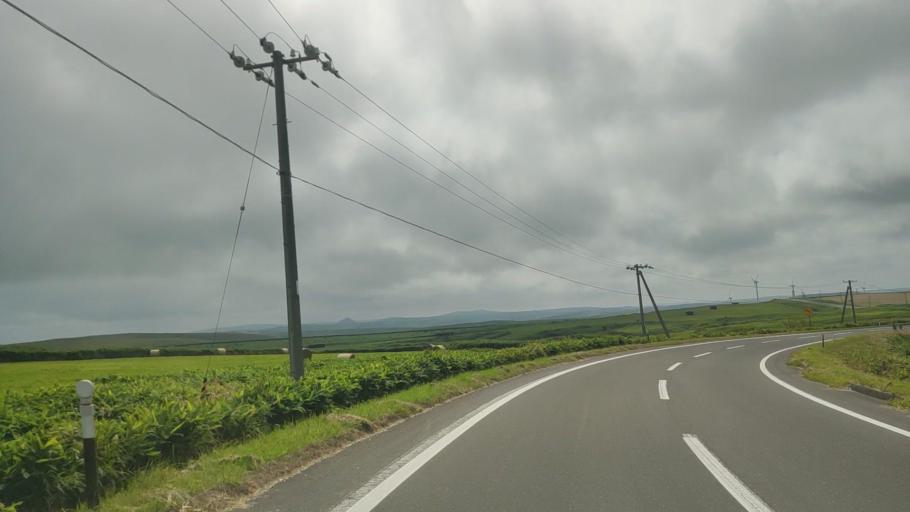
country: JP
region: Hokkaido
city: Makubetsu
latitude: 45.4930
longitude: 141.9373
